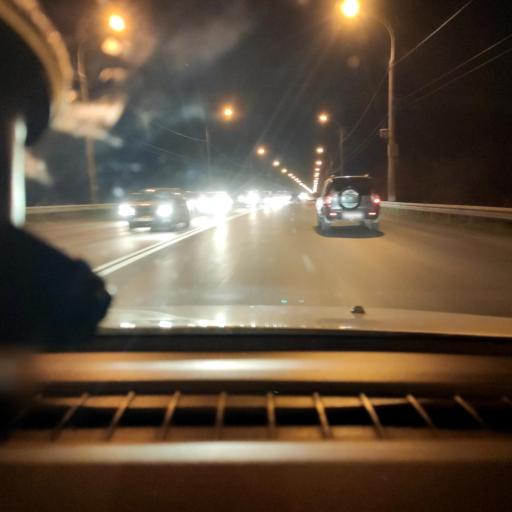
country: RU
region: Samara
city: Samara
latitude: 53.1646
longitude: 50.1966
